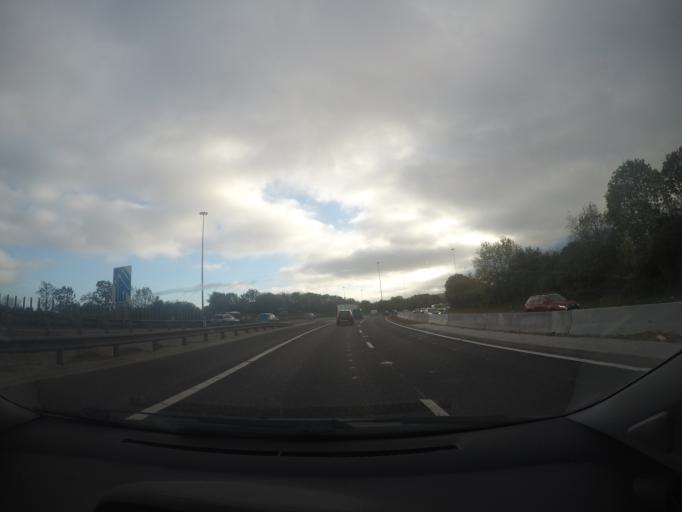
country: GB
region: England
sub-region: City and Borough of Leeds
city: Leeds
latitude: 53.7783
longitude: -1.5375
